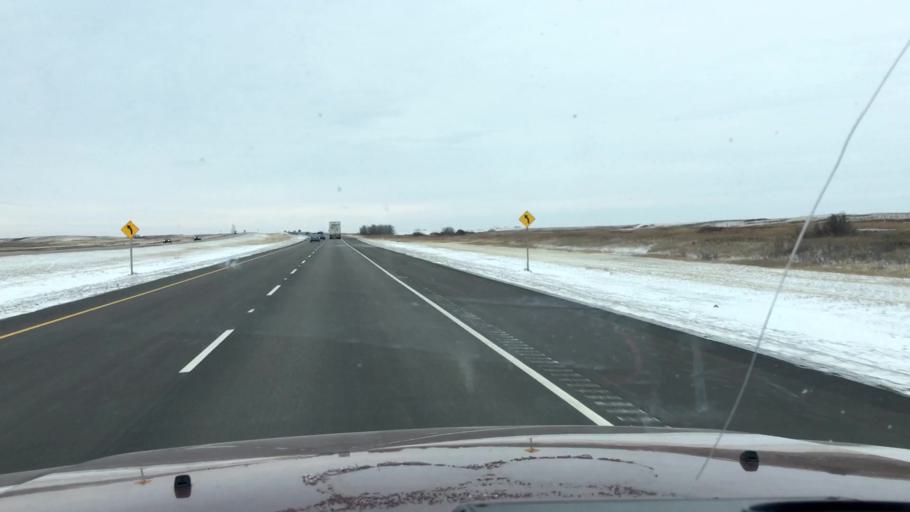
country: CA
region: Saskatchewan
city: Moose Jaw
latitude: 50.8872
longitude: -105.6233
